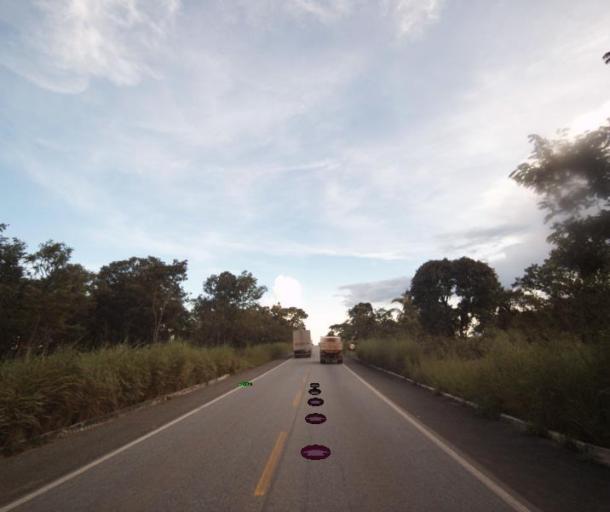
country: BR
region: Goias
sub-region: Uruacu
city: Uruacu
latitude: -14.2451
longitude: -49.1381
